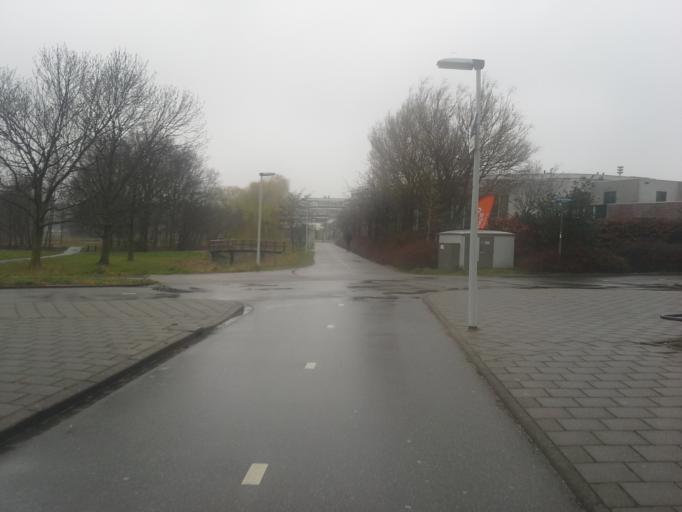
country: NL
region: South Holland
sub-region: Gemeente Voorschoten
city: Voorschoten
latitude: 52.1497
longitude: 4.4544
